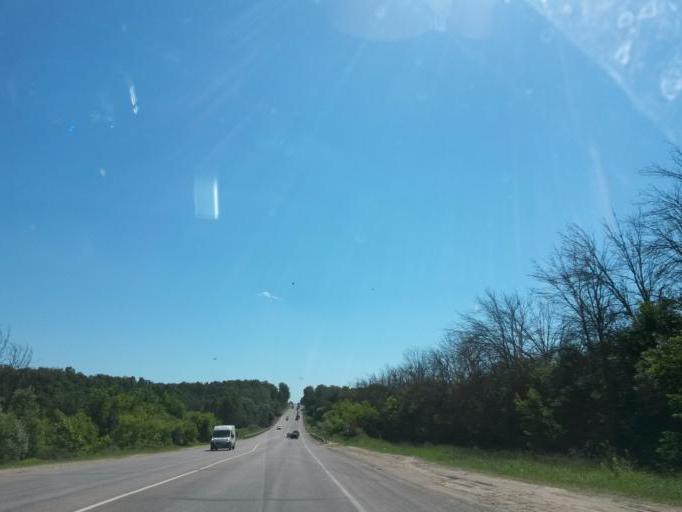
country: RU
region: Moskovskaya
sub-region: Chekhovskiy Rayon
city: Chekhov
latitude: 55.1124
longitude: 37.4474
